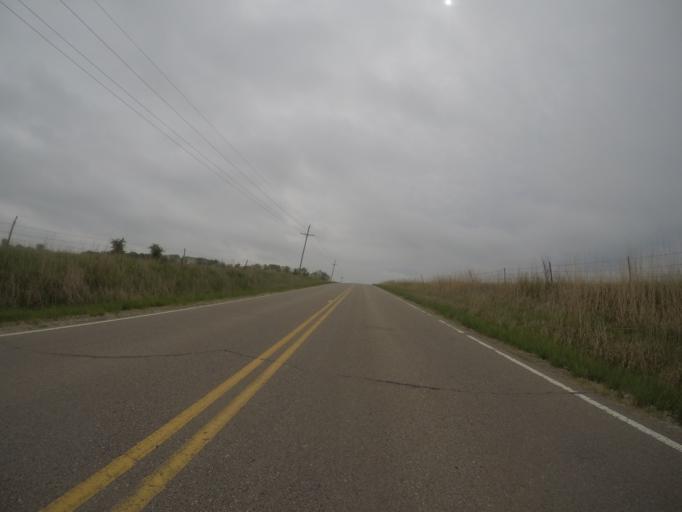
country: US
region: Kansas
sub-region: Pottawatomie County
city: Westmoreland
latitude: 39.5223
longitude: -96.2554
